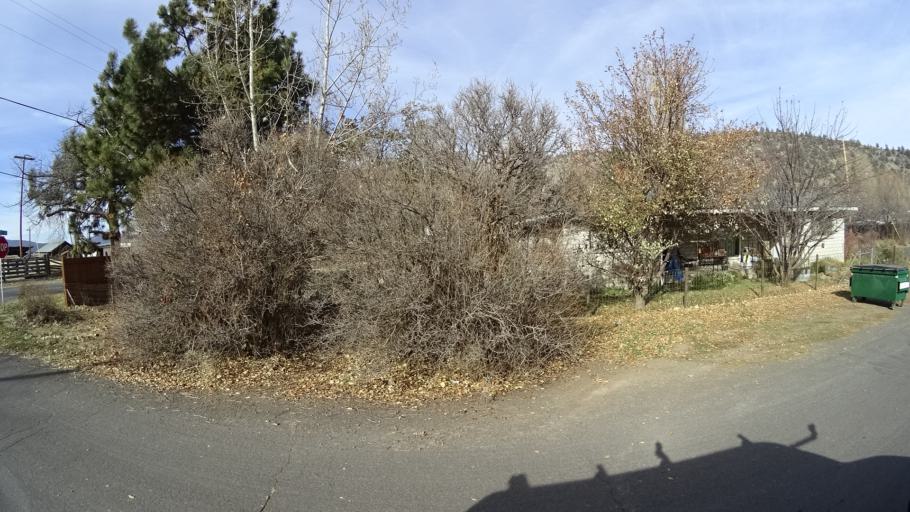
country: US
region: Oregon
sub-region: Klamath County
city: Klamath Falls
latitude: 41.9701
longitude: -121.9212
